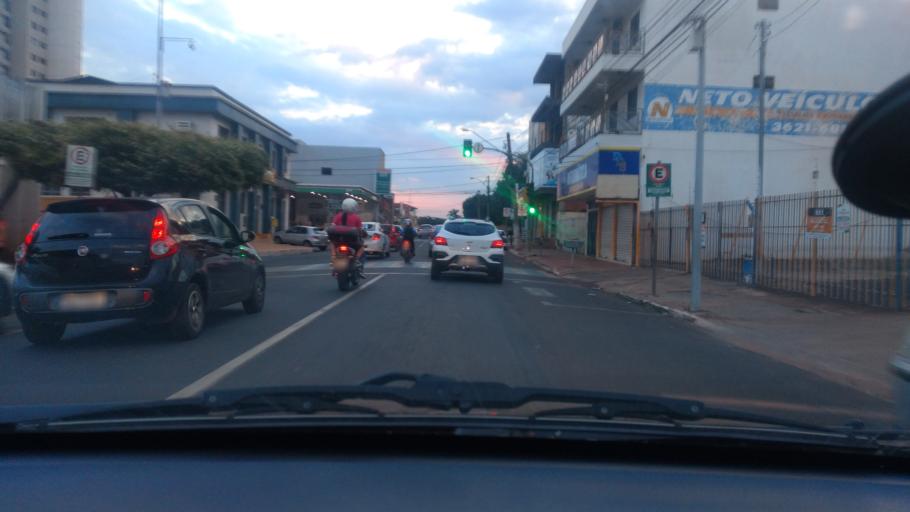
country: BR
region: Goias
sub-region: Santa Helena De Goias
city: Santa Helena de Goias
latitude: -17.7961
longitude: -50.9294
